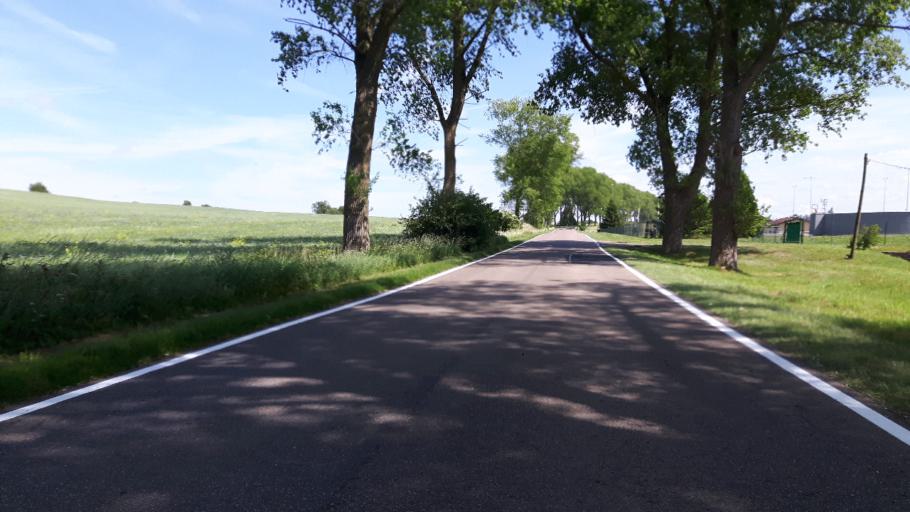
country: PL
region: Pomeranian Voivodeship
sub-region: Powiat wejherowski
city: Gniewino
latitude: 54.7204
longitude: 17.9904
